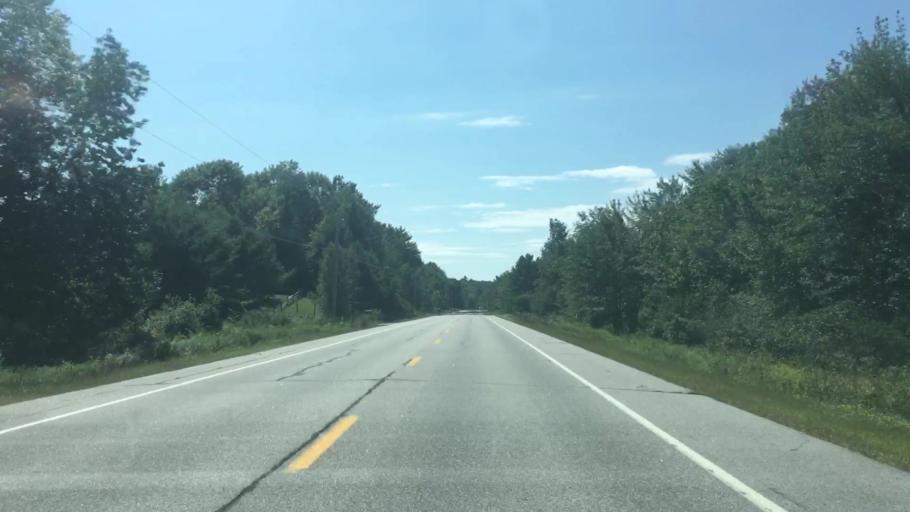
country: US
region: Maine
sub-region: Androscoggin County
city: Sabattus
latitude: 44.1439
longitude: -70.0443
